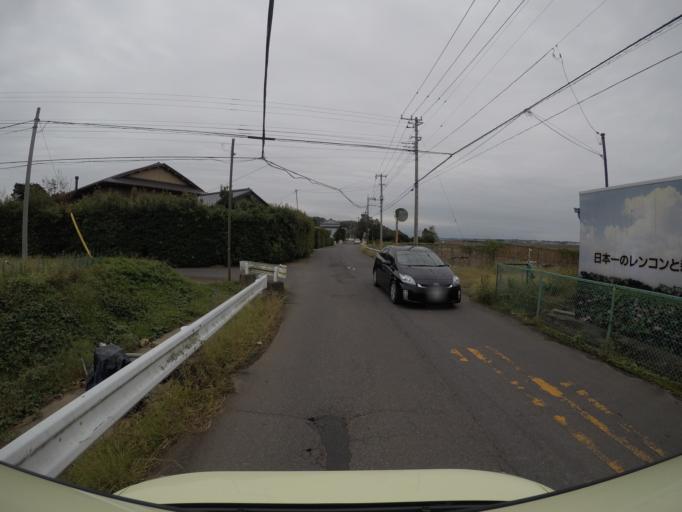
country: JP
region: Ibaraki
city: Ami
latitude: 36.0902
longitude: 140.2409
